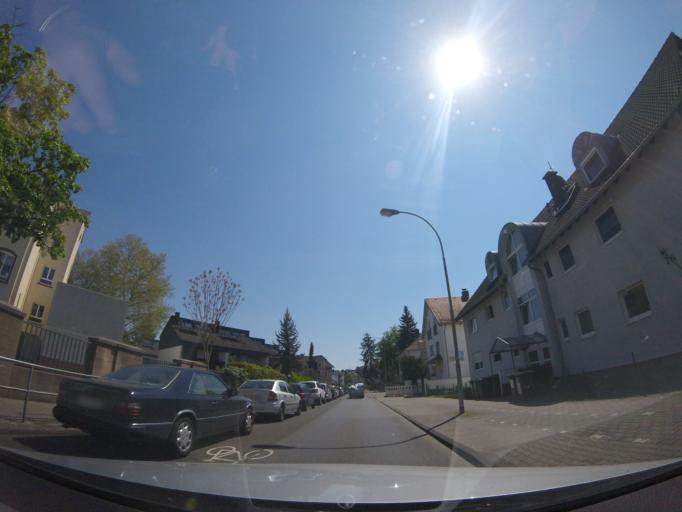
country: DE
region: Hesse
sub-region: Regierungsbezirk Darmstadt
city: Offenbach
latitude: 50.1263
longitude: 8.7656
